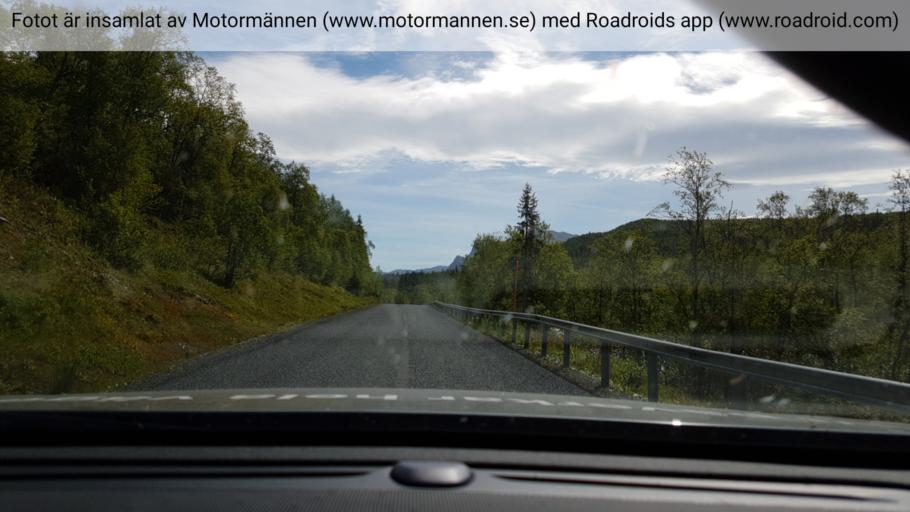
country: SE
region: Vaesterbotten
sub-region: Vilhelmina Kommun
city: Sjoberg
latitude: 65.2773
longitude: 15.3181
